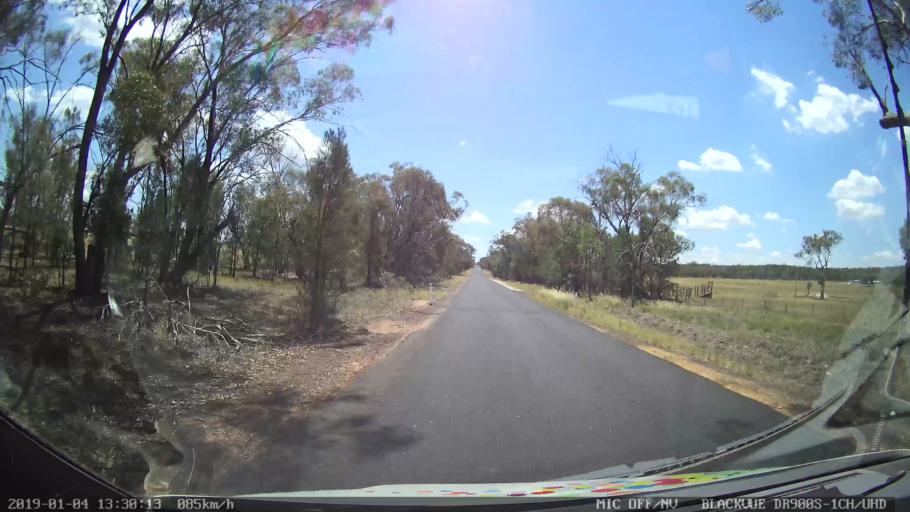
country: AU
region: New South Wales
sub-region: Parkes
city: Peak Hill
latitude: -32.6379
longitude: 148.5496
